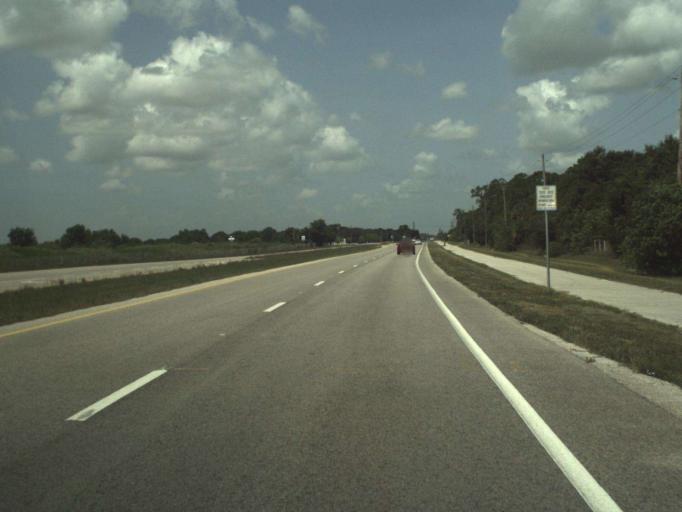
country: US
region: Florida
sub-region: Saint Lucie County
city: Fort Pierce South
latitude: 27.4093
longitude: -80.4205
